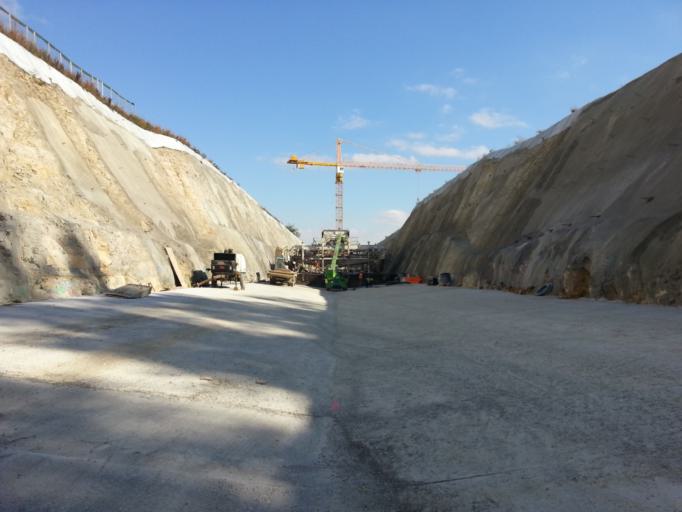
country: DE
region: Baden-Wuerttemberg
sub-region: Tuebingen Region
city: Laichingen
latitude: 48.5288
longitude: 9.7073
